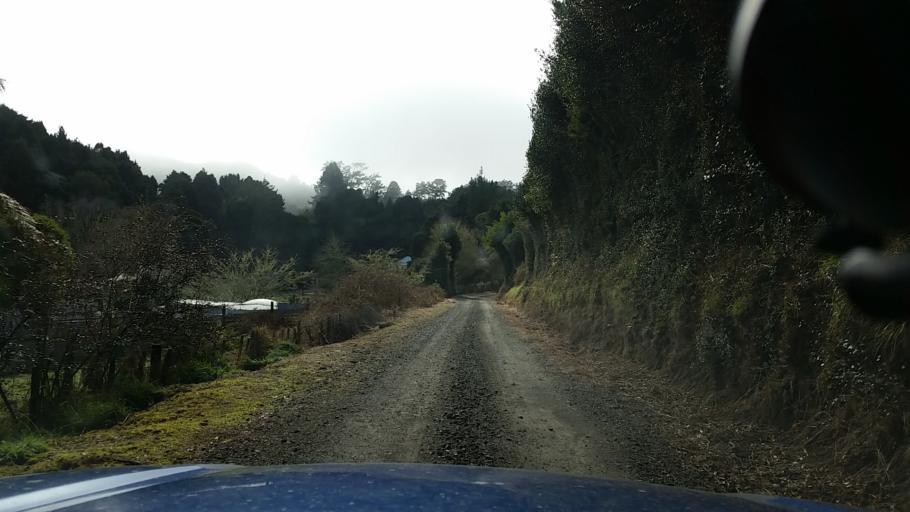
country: NZ
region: Taranaki
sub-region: New Plymouth District
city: Waitara
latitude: -39.0331
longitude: 174.8005
